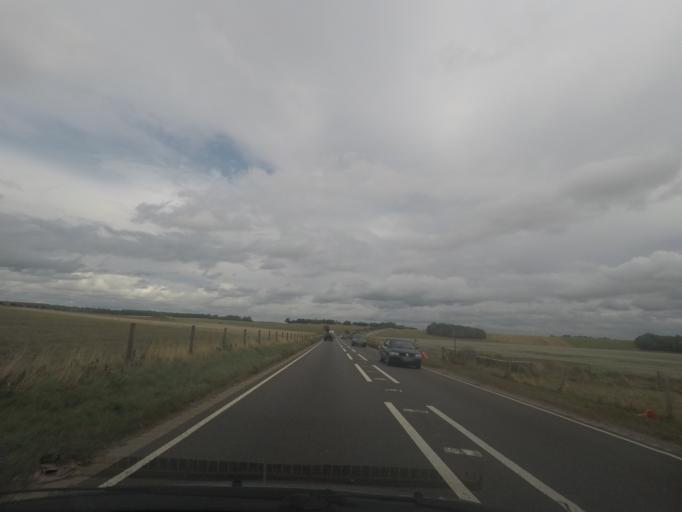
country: GB
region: England
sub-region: Wiltshire
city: Durnford
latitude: 51.1768
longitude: -1.8281
